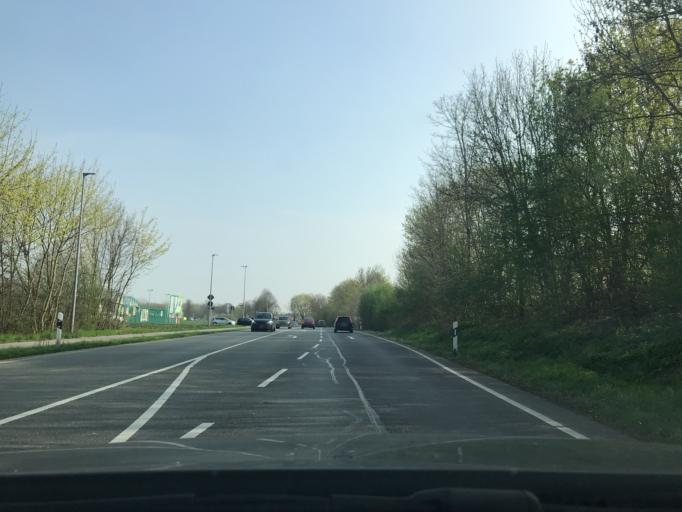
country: DE
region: North Rhine-Westphalia
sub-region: Regierungsbezirk Dusseldorf
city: Goch
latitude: 51.6663
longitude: 6.1710
